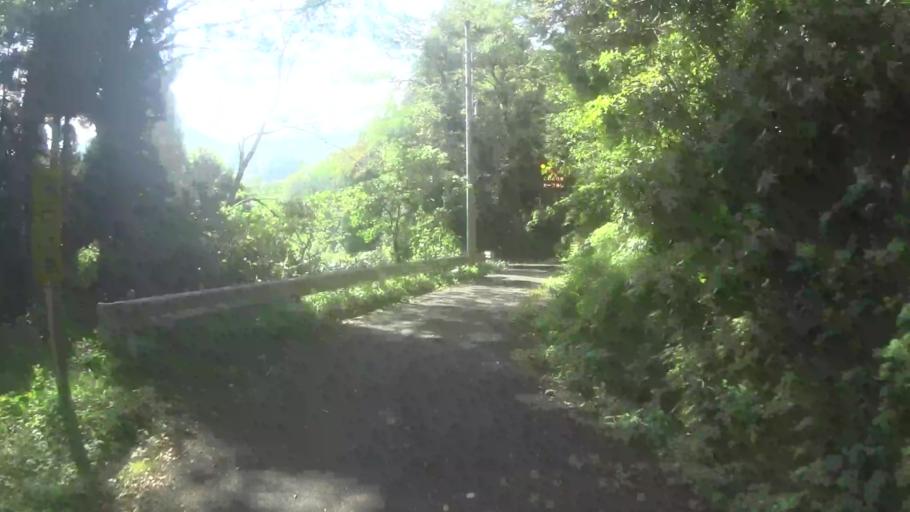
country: JP
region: Kyoto
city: Miyazu
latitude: 35.7122
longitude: 135.1627
